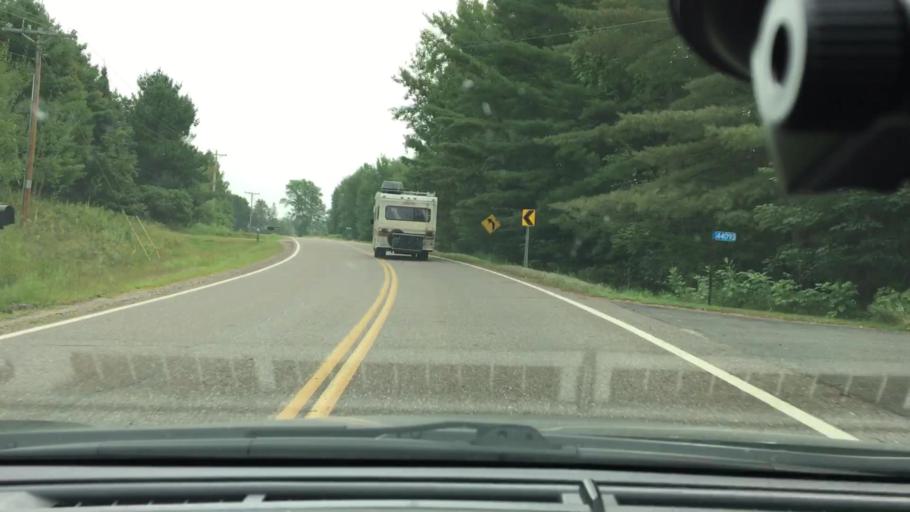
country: US
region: Minnesota
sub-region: Aitkin County
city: Aitkin
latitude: 46.4014
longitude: -93.7731
